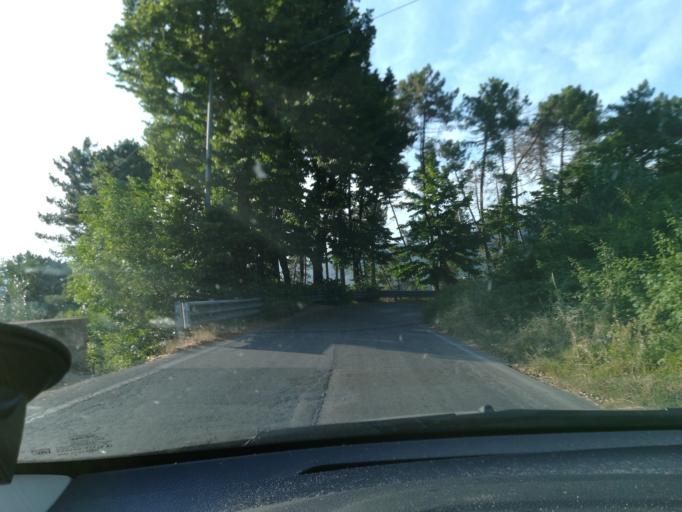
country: IT
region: Tuscany
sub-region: Provincia di Lucca
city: Stiava
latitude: 43.9174
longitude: 10.3390
